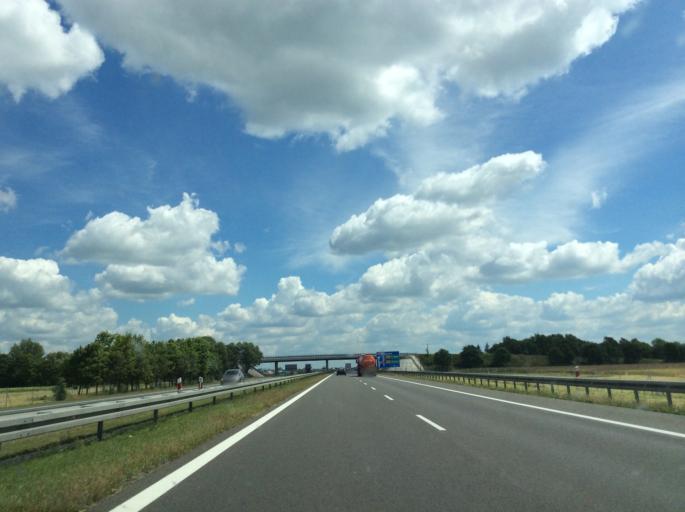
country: PL
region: Greater Poland Voivodeship
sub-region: Powiat koninski
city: Rzgow Pierwszy
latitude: 52.2083
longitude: 18.0063
